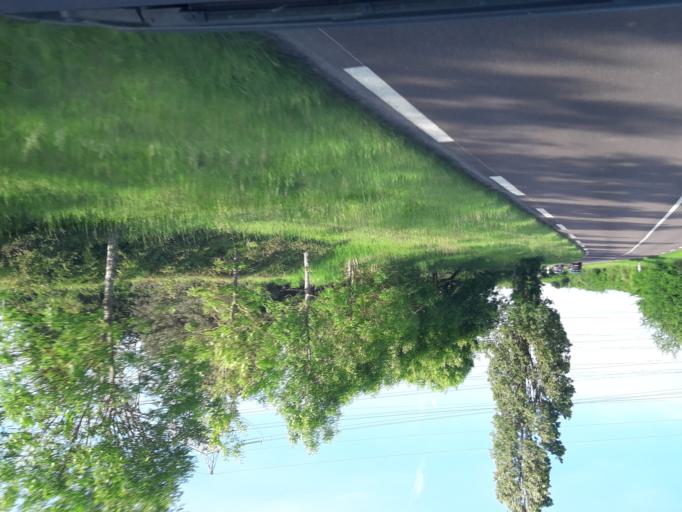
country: FR
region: Ile-de-France
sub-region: Departement de l'Essonne
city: Saint-Vrain
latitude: 48.5499
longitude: 2.3172
